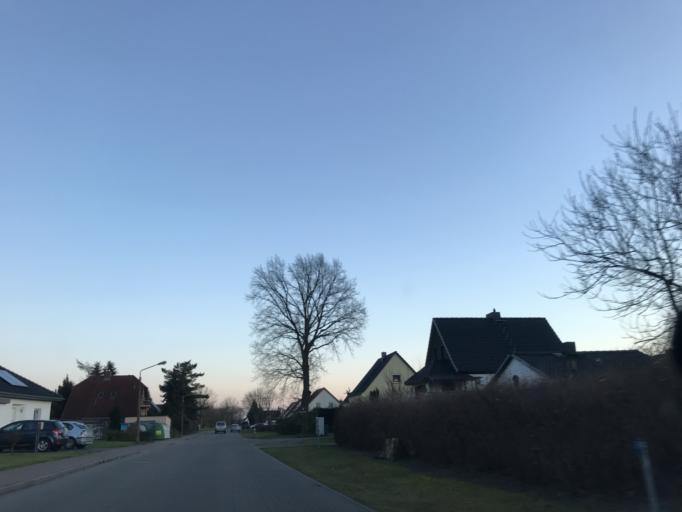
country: DE
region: Brandenburg
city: Premnitz
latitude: 52.5252
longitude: 12.3499
